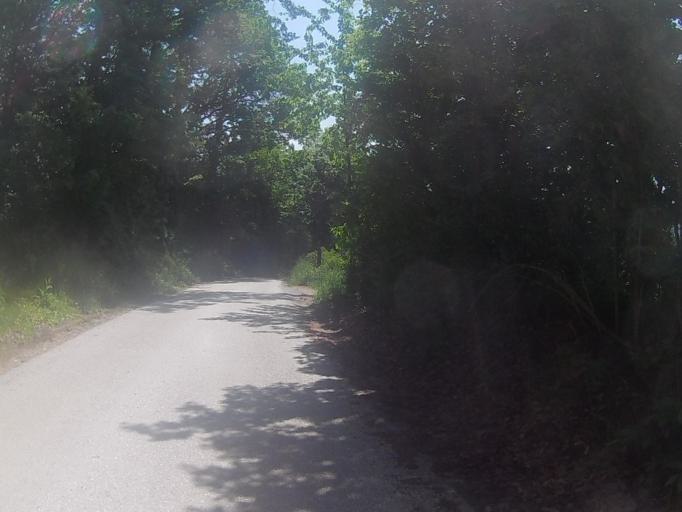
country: SI
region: Sveti Jurij v Slovenskih Goricah
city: Jurovski Dol
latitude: 46.5972
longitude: 15.7313
